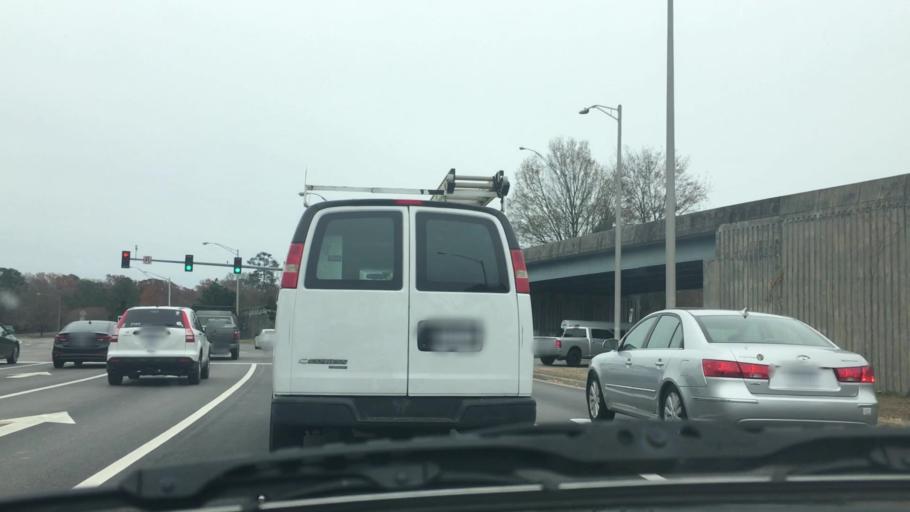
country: US
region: Virginia
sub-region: City of Chesapeake
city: Chesapeake
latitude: 36.8311
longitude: -76.1377
